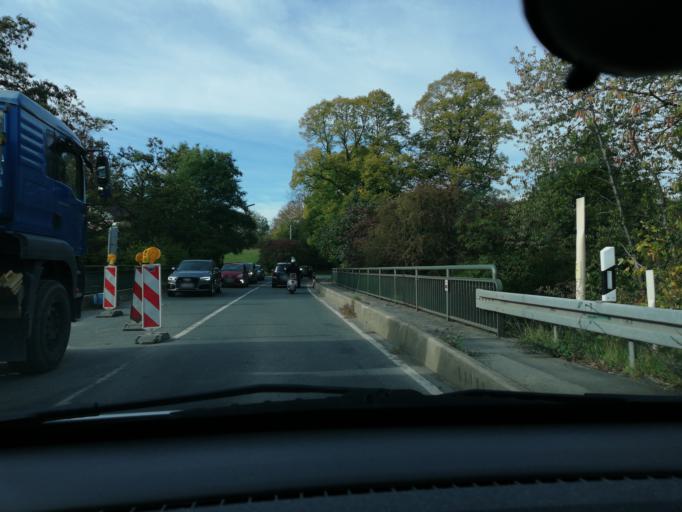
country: DE
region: North Rhine-Westphalia
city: Sprockhovel
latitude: 51.3324
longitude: 7.2621
